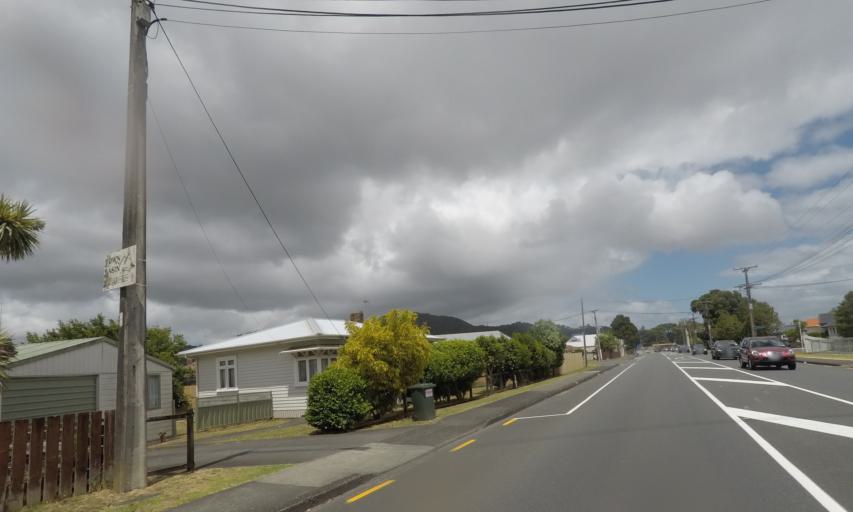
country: NZ
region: Northland
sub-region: Whangarei
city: Whangarei
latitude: -35.7059
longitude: 174.3197
